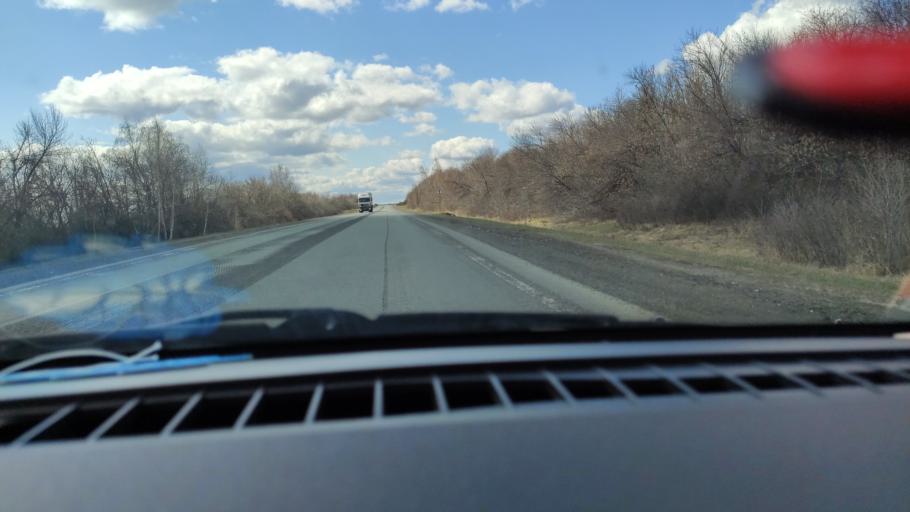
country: RU
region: Saratov
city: Dukhovnitskoye
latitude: 52.6359
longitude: 48.1879
